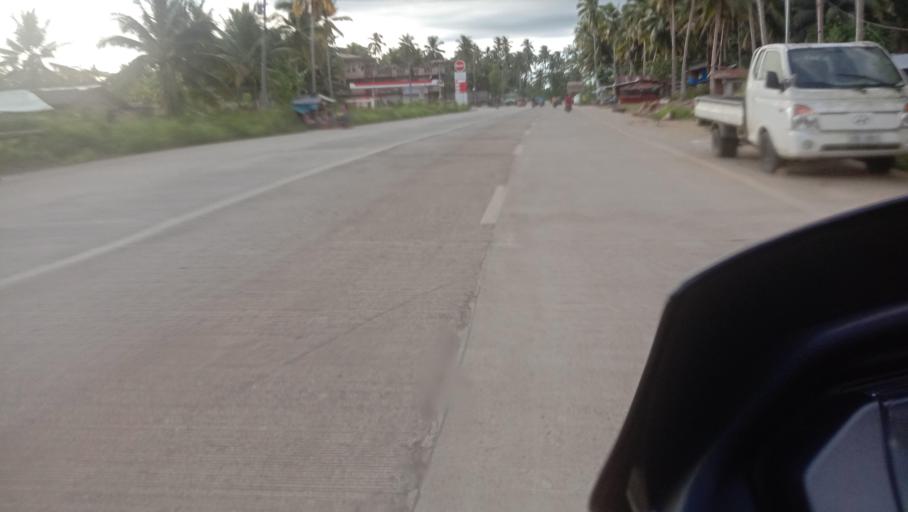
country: PH
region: Caraga
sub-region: Province of Surigao del Sur
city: Barobo
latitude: 8.5205
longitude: 126.1213
